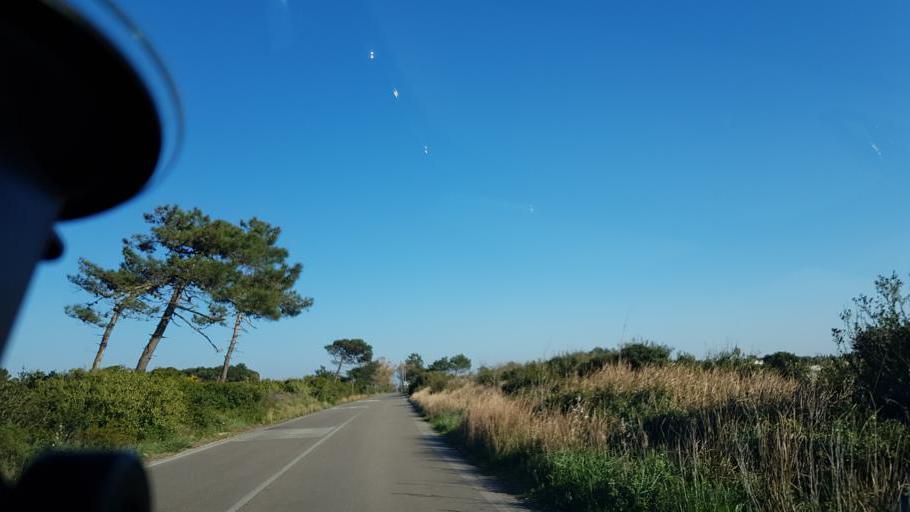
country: IT
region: Apulia
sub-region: Provincia di Lecce
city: Giorgilorio
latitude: 40.4560
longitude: 18.2121
